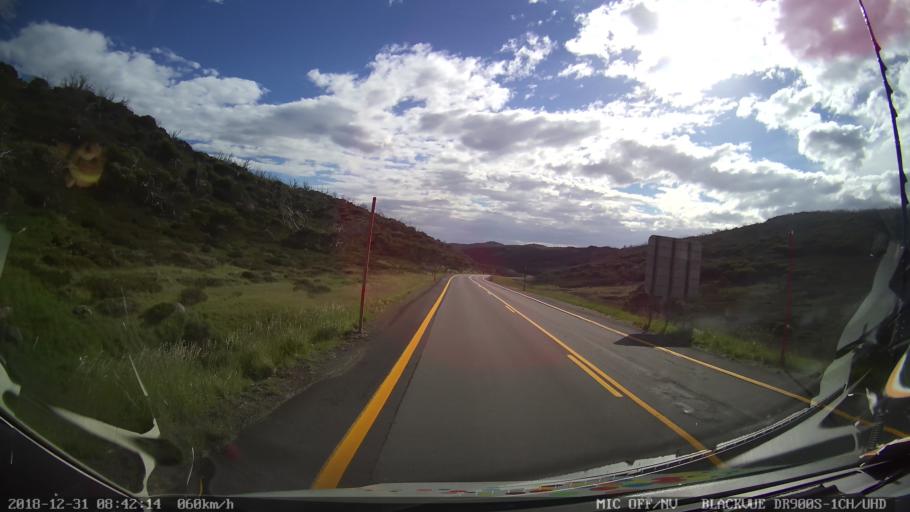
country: AU
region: New South Wales
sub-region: Snowy River
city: Jindabyne
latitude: -36.3943
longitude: 148.4299
